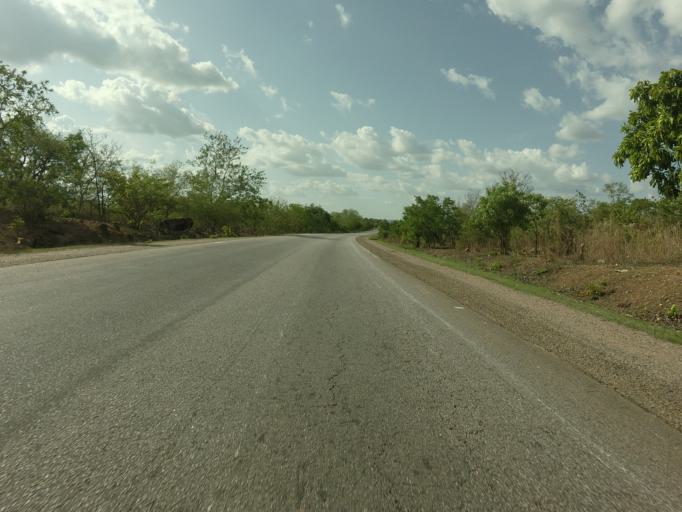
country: GH
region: Upper East
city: Bolgatanga
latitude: 10.5640
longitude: -0.8338
